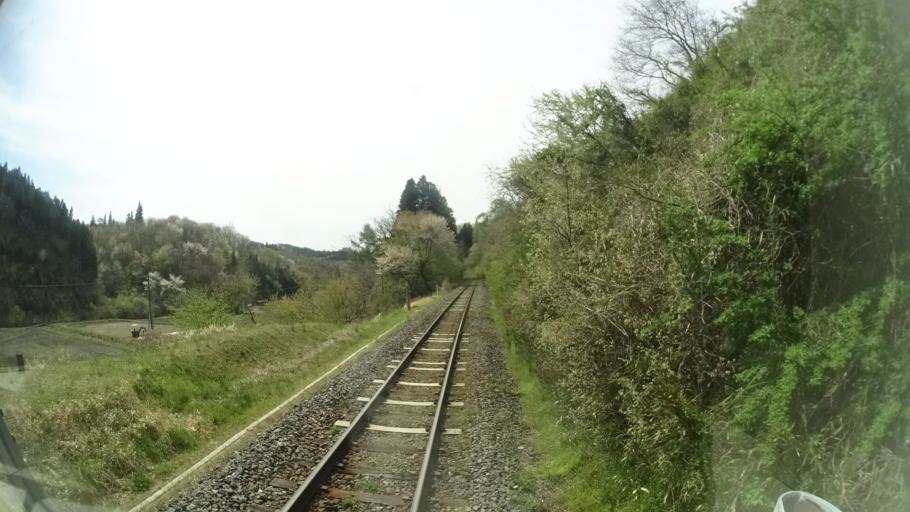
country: JP
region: Iwate
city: Ichinoseki
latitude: 38.9878
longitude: 141.3317
